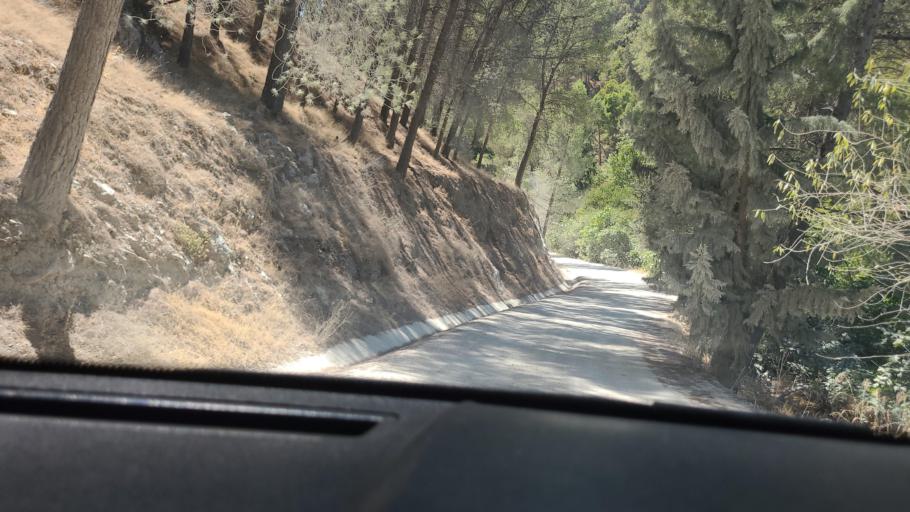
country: ES
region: Andalusia
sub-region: Provincia de Jaen
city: Belmez de la Moraleda
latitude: 37.7888
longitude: -3.4078
